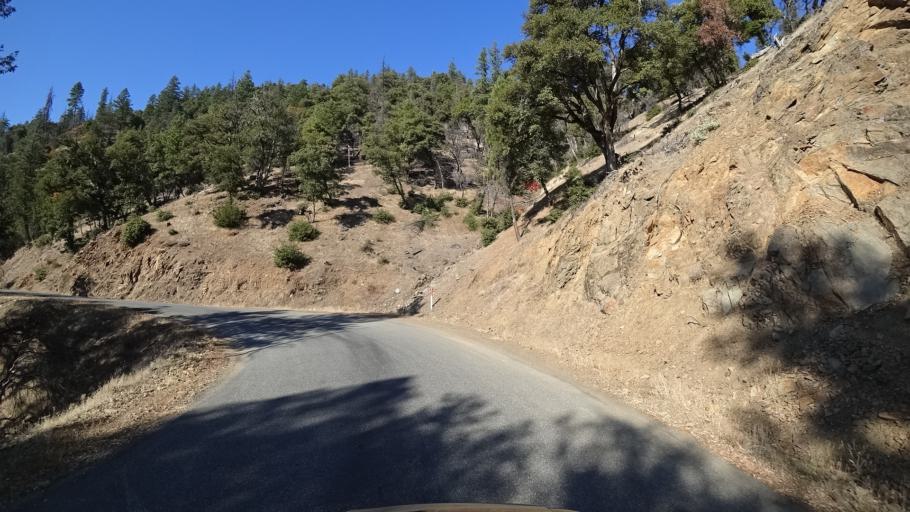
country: US
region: California
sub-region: Siskiyou County
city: Happy Camp
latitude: 41.7100
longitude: -123.0300
